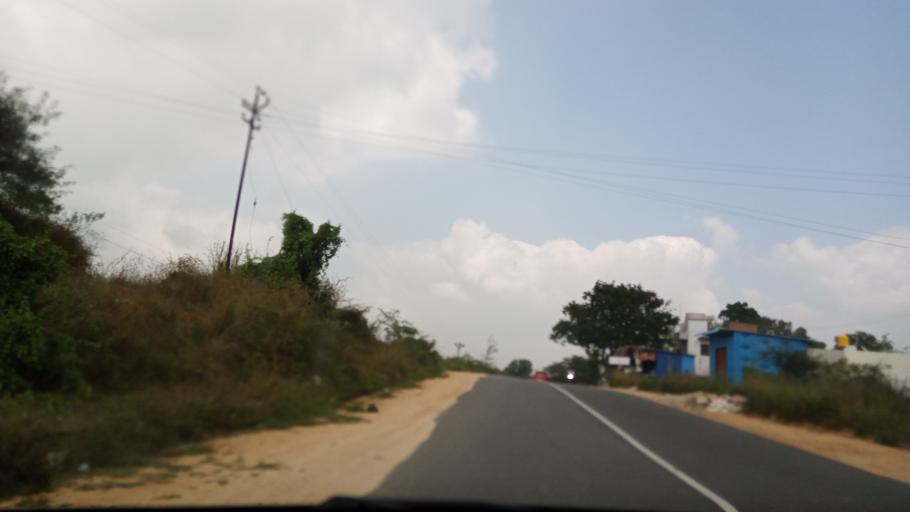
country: IN
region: Andhra Pradesh
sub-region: Chittoor
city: Madanapalle
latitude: 13.5903
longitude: 78.5257
